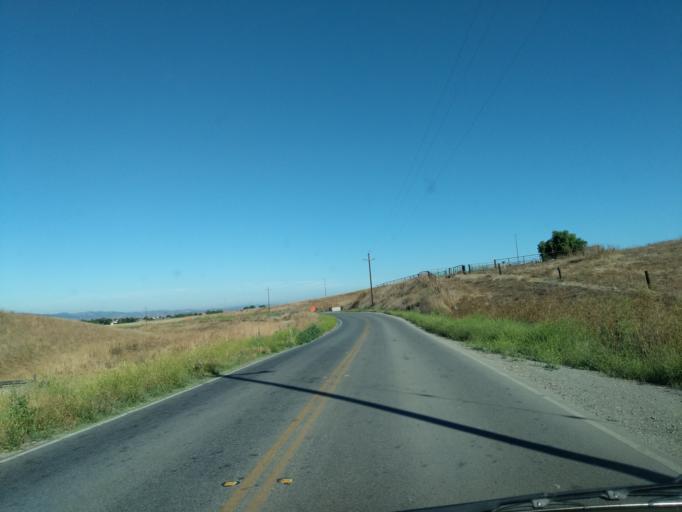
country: US
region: California
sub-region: San Benito County
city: Ridgemark
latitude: 36.8273
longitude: -121.3339
